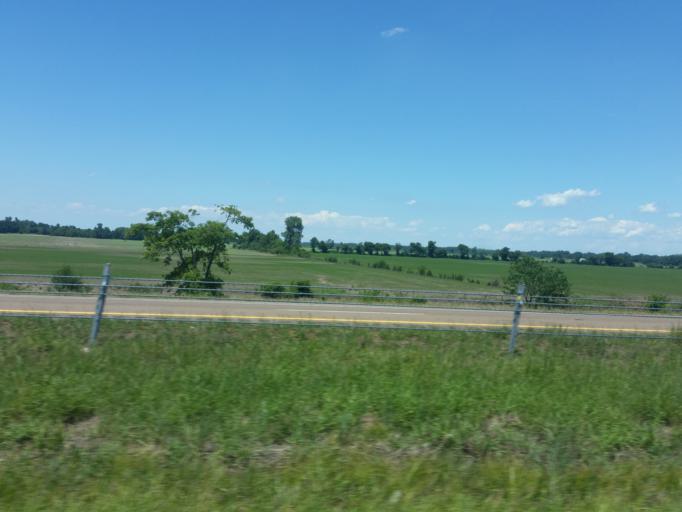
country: US
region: Missouri
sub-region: Pemiscot County
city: Caruthersville
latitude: 36.0956
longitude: -89.5974
